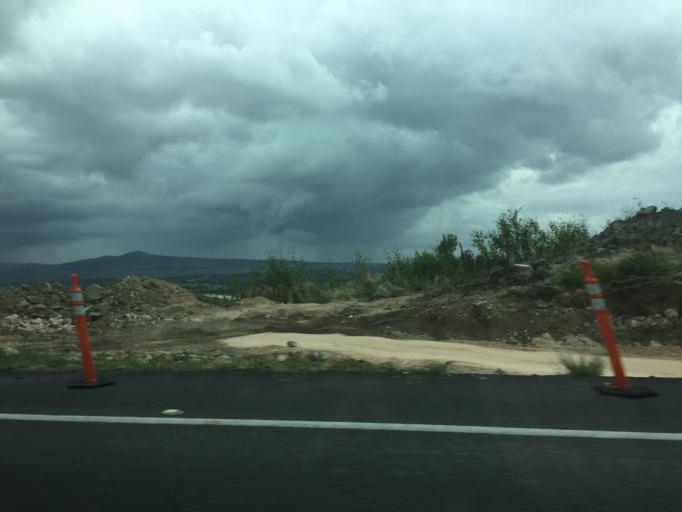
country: MX
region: Jalisco
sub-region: Zapotlanejo
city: La Mezquitera
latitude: 20.5847
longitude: -103.0976
